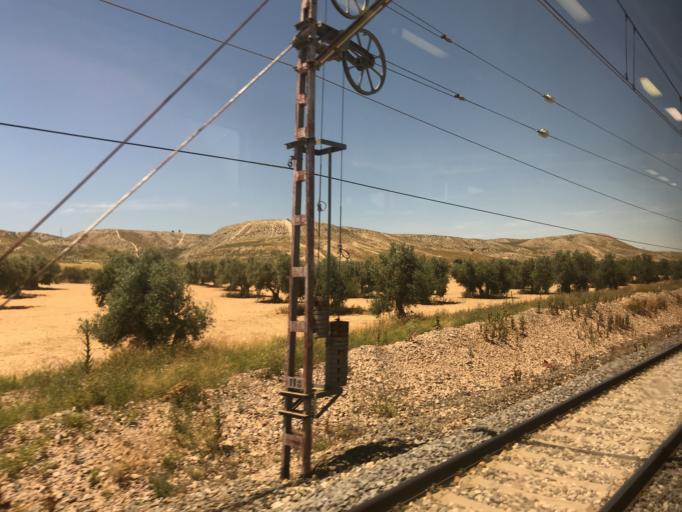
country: ES
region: Madrid
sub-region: Provincia de Madrid
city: Ciempozuelos
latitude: 40.1238
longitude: -3.6177
